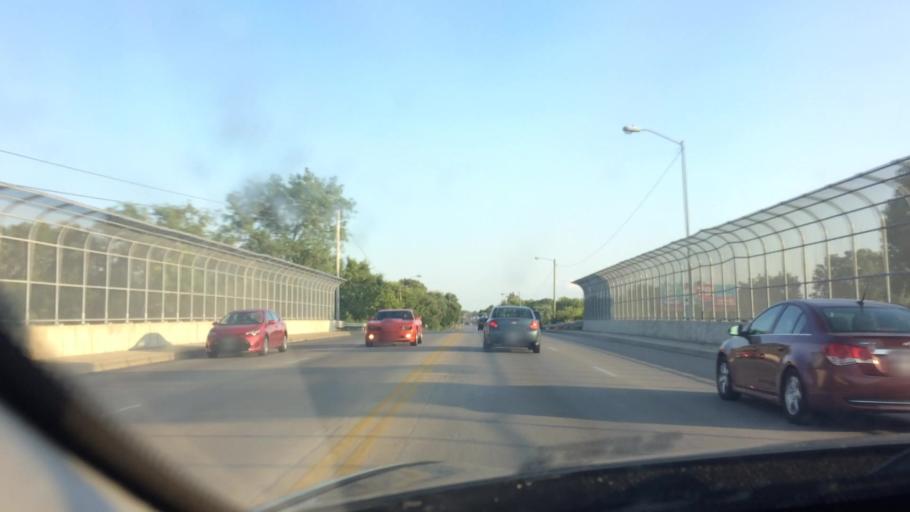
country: US
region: Ohio
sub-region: Lucas County
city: Ottawa Hills
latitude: 41.6312
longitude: -83.6259
